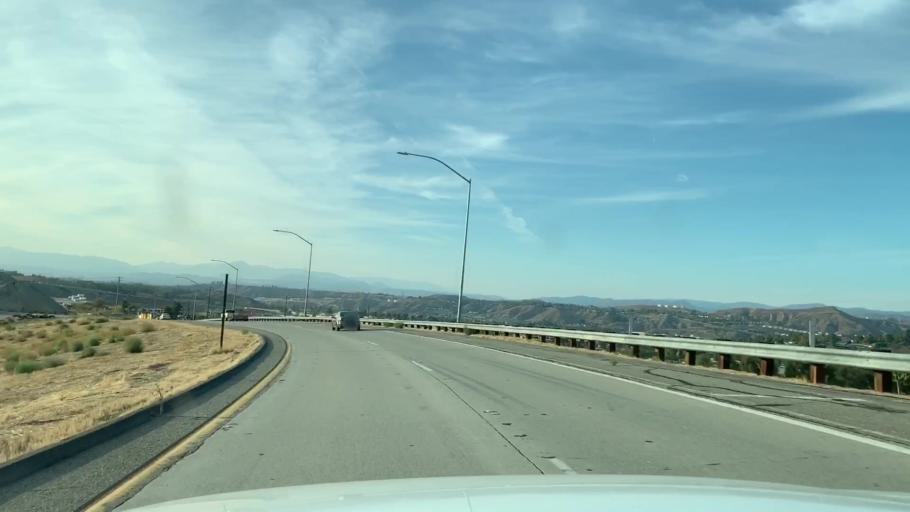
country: US
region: California
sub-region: Los Angeles County
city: Santa Clarita
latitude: 34.4051
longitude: -118.4574
